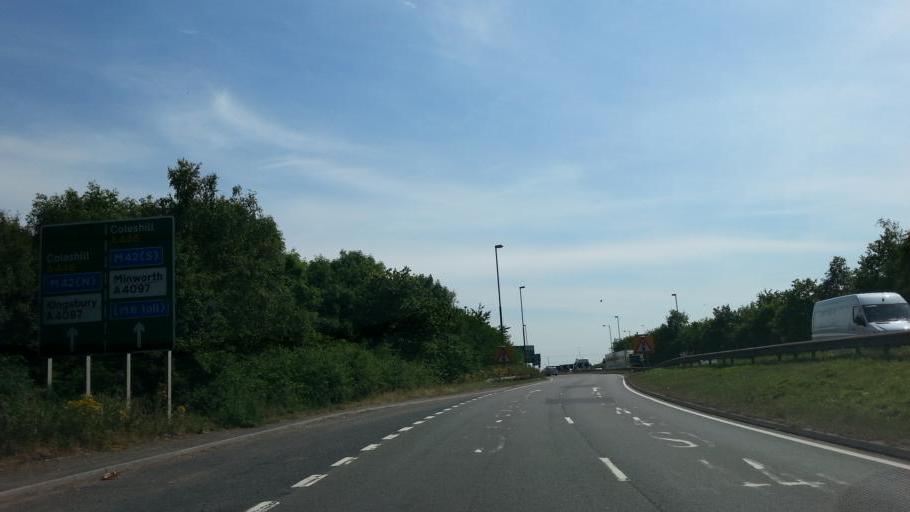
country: GB
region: England
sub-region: Warwickshire
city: Curdworth
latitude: 52.5413
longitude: -1.7271
